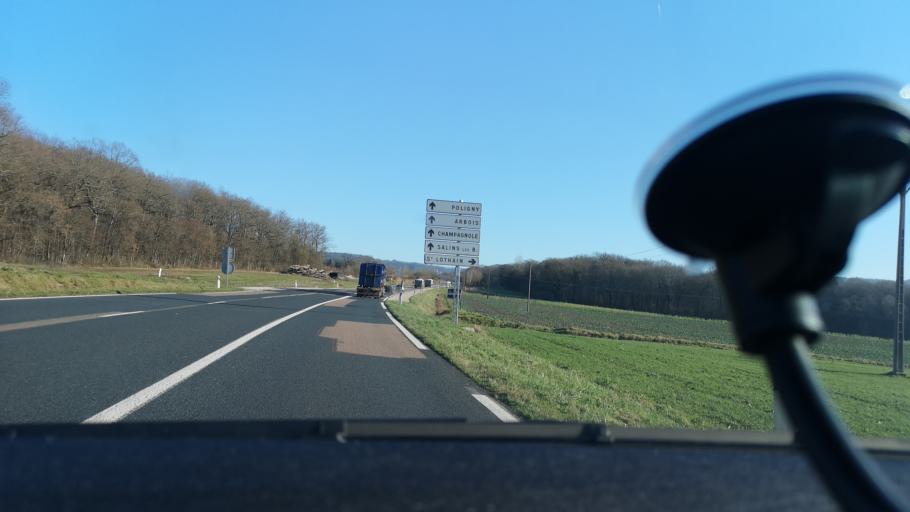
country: FR
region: Franche-Comte
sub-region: Departement du Jura
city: Poligny
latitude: 46.8450
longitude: 5.6476
